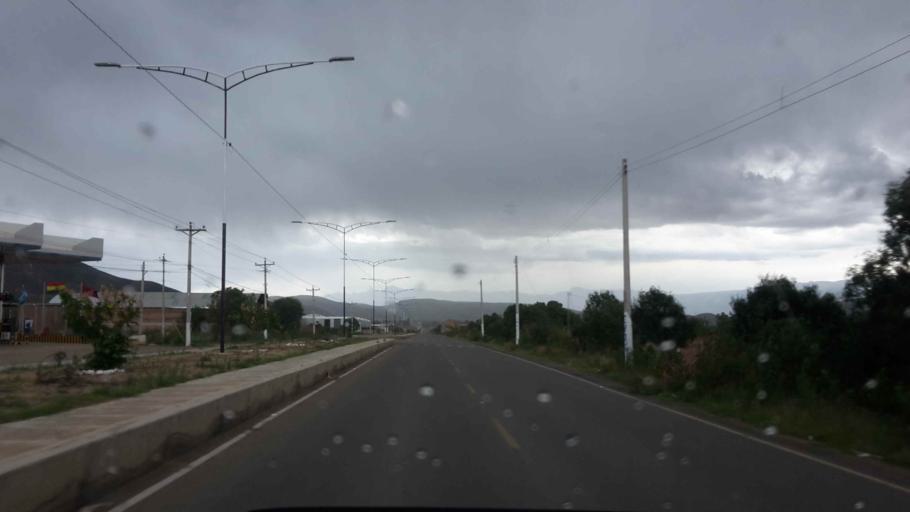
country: BO
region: Cochabamba
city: Tarata
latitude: -17.6033
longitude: -66.0324
